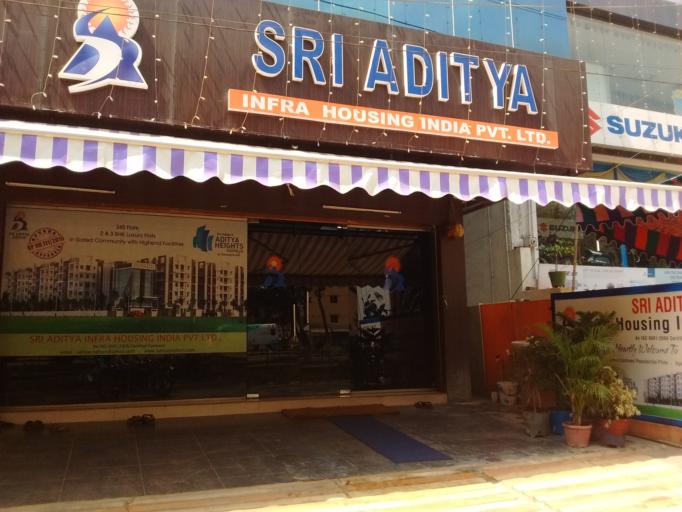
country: IN
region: Andhra Pradesh
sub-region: Krishna
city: Yanamalakuduru
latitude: 16.5130
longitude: 80.6678
